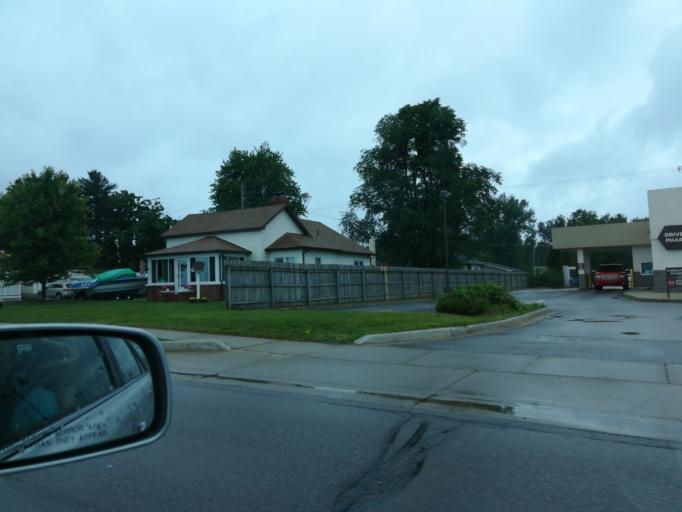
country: US
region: Michigan
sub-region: Iosco County
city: Tawas City
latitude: 44.2733
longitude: -83.5099
